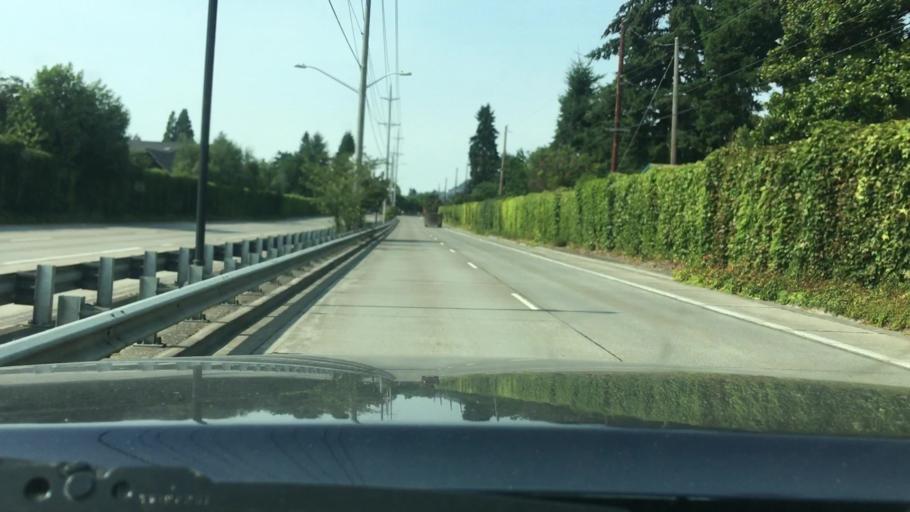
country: US
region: Oregon
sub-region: Lane County
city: Springfield
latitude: 44.0737
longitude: -123.0299
